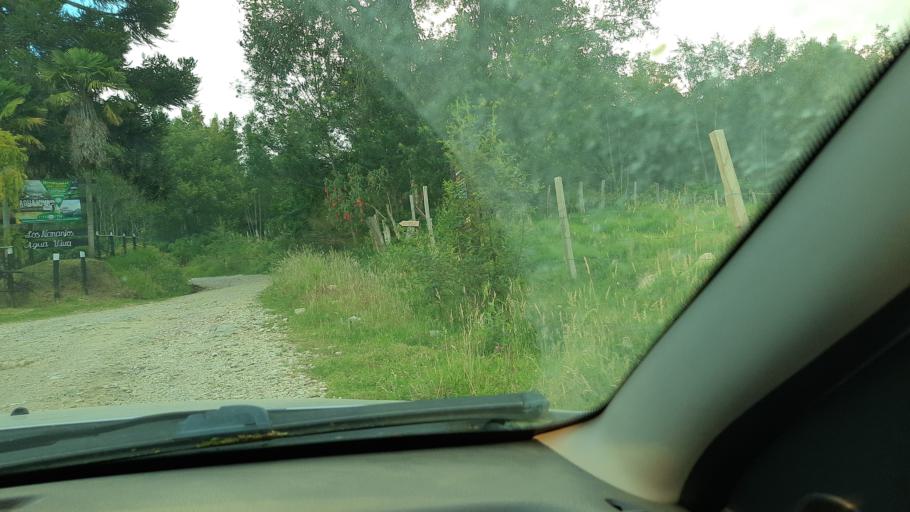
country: CO
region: Boyaca
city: La Capilla
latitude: 5.7224
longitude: -73.4717
